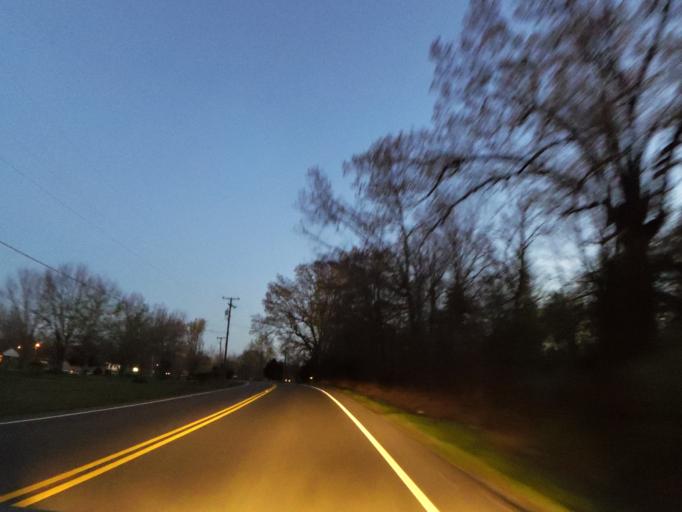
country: US
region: Tennessee
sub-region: Robertson County
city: Greenbrier
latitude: 36.3659
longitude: -86.8880
